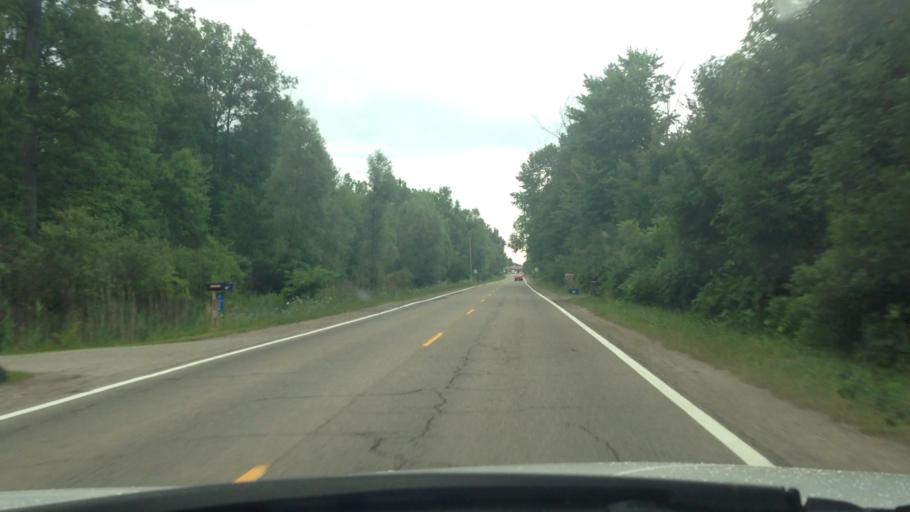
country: US
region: Michigan
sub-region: Oakland County
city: Clarkston
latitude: 42.7295
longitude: -83.3498
